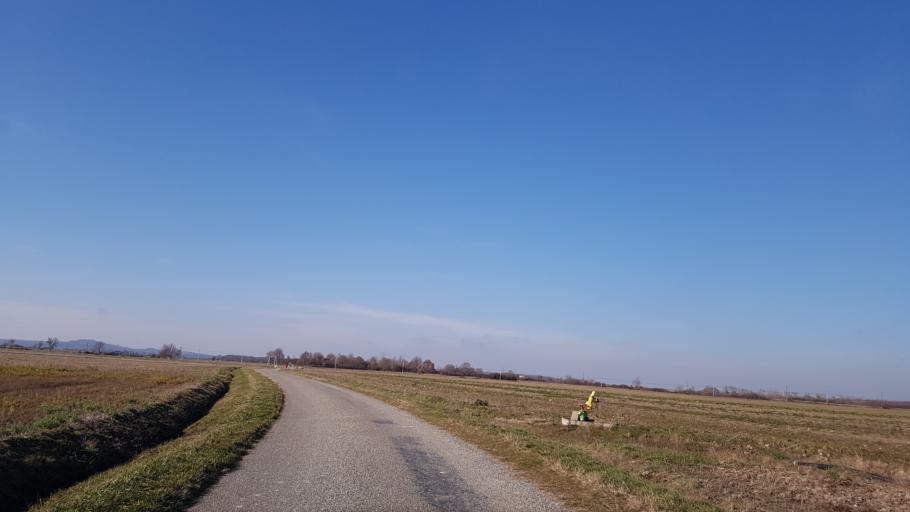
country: FR
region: Midi-Pyrenees
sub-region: Departement de l'Ariege
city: La Tour-du-Crieu
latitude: 43.1536
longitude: 1.6938
